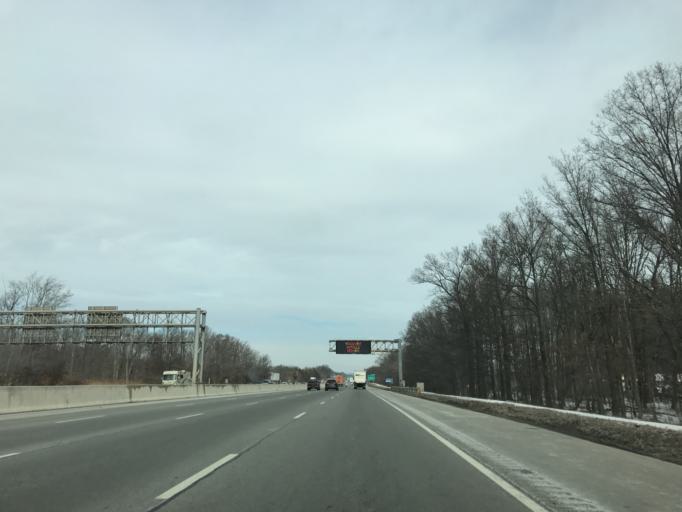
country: US
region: New Jersey
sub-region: Morris County
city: Parsippany
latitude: 40.8404
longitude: -74.4326
